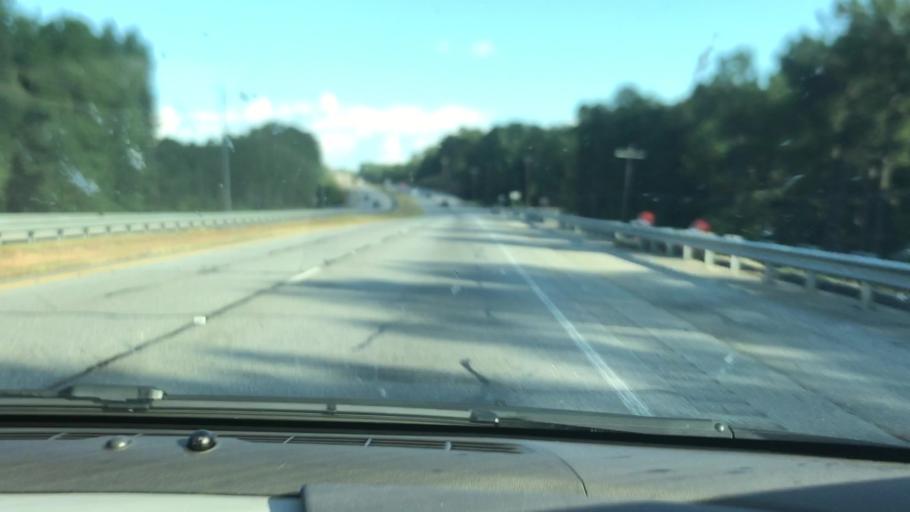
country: US
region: Georgia
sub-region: Muscogee County
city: Columbus
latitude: 32.3936
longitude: -84.8860
